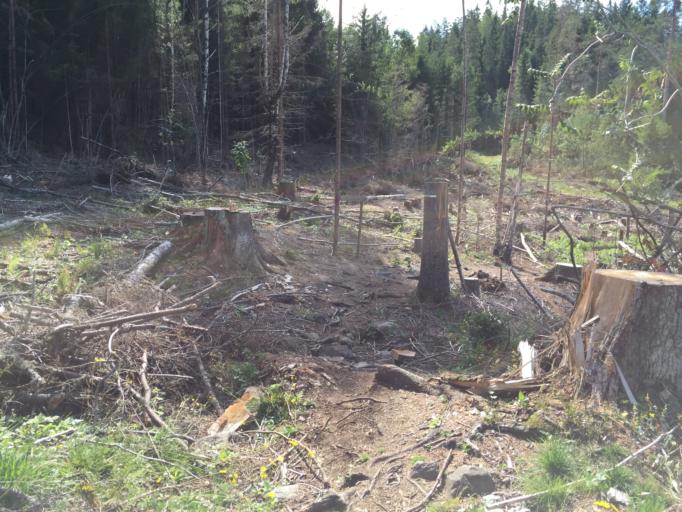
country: NO
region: Akershus
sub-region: Skedsmo
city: Lillestrom
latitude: 59.9258
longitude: 11.0206
